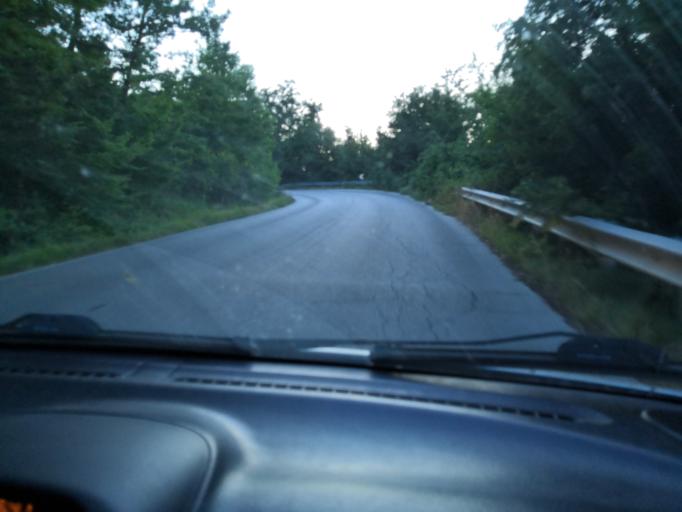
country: IT
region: Molise
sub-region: Provincia di Campobasso
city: Jelsi
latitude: 41.5107
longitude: 14.7820
